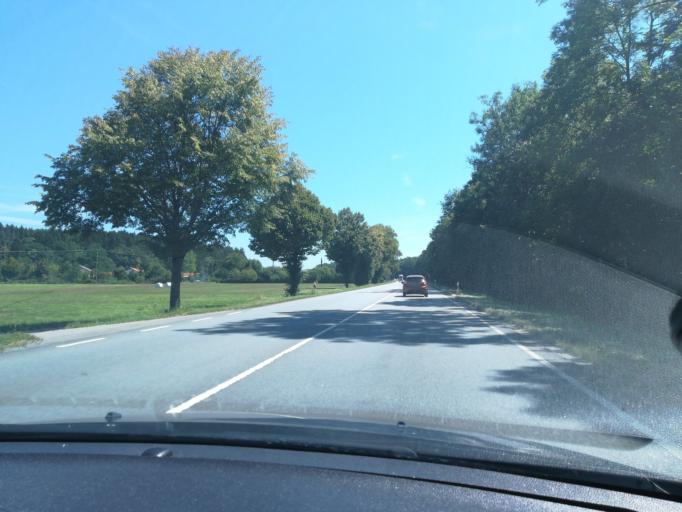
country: DE
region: Bavaria
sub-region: Upper Bavaria
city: Forstern
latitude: 48.1596
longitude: 11.9522
